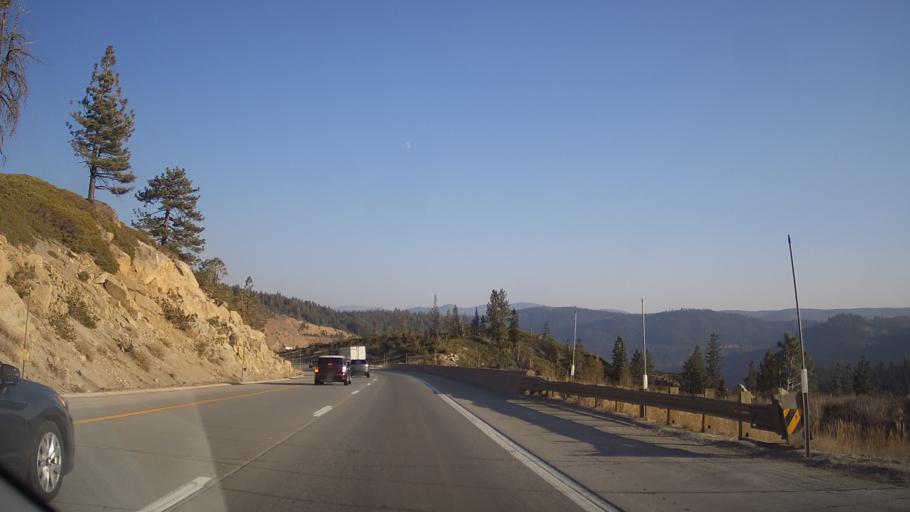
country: US
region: California
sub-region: Nevada County
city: Truckee
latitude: 39.3417
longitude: -120.3230
